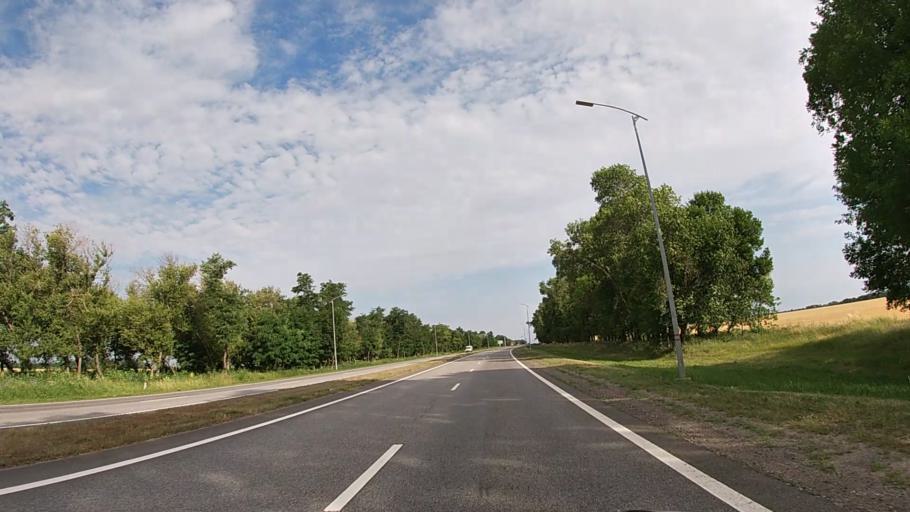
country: RU
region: Belgorod
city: Tomarovka
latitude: 50.6746
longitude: 36.2955
